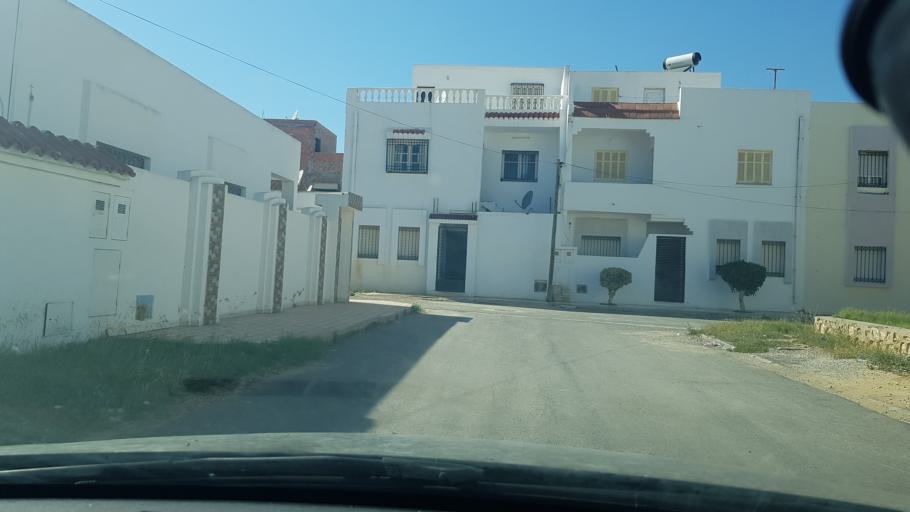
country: TN
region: Safaqis
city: Al Qarmadah
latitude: 34.8253
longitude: 10.7568
